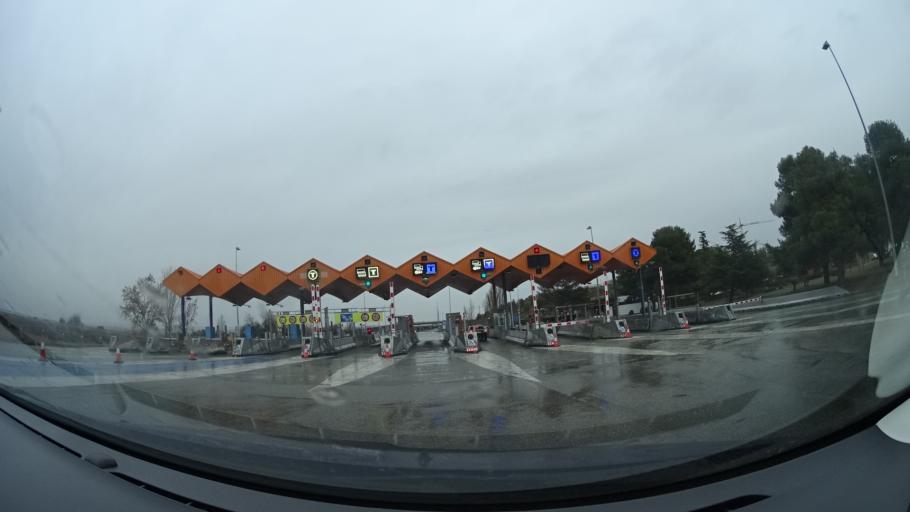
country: ES
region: Catalonia
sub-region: Provincia de Lleida
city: Alfes
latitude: 41.5576
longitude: 0.6209
